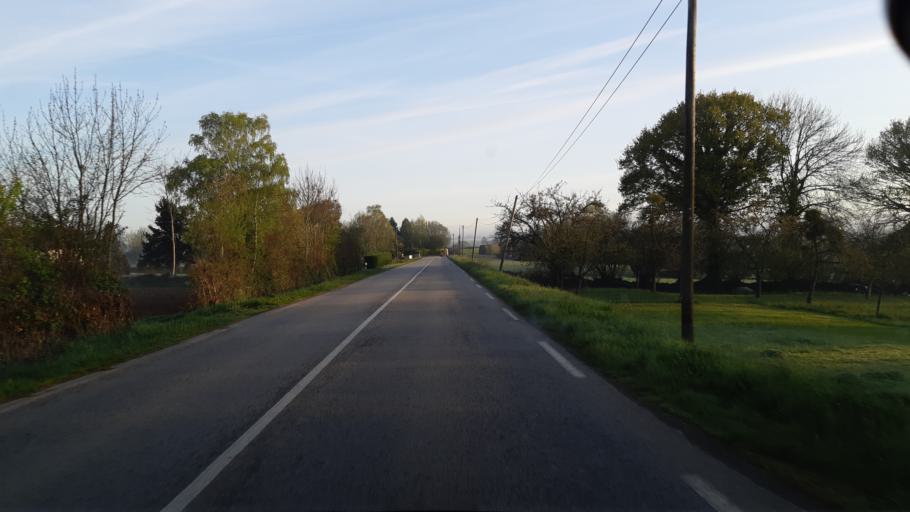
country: FR
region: Lower Normandy
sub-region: Departement de la Manche
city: Agneaux
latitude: 49.0564
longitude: -1.1326
